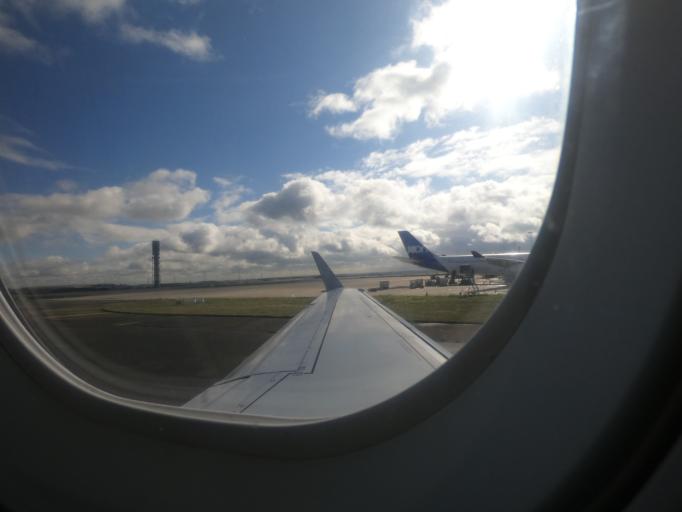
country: FR
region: Ile-de-France
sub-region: Departement de Seine-et-Marne
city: Mitry-Mory
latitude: 49.0088
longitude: 2.5914
